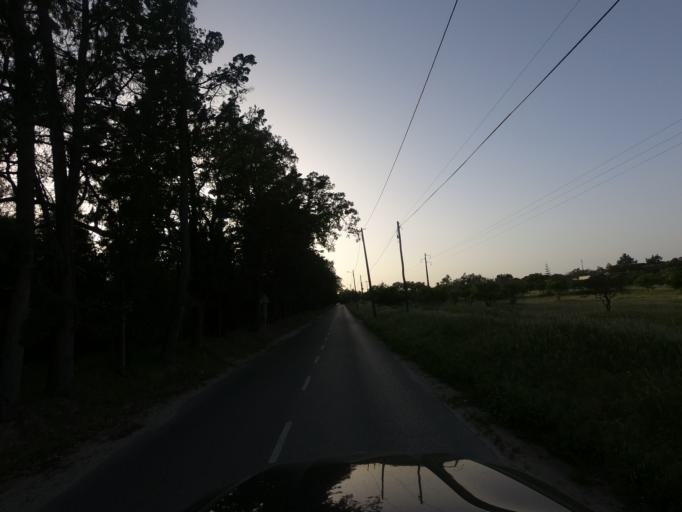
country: PT
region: Setubal
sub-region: Setubal
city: Setubal
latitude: 38.5339
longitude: -8.8162
